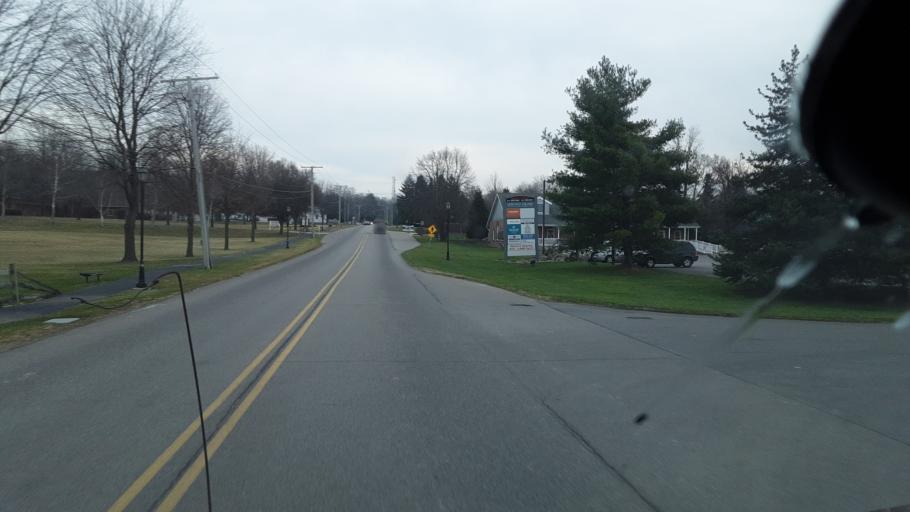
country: US
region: Indiana
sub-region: Elkhart County
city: Middlebury
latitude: 41.6685
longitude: -85.7186
